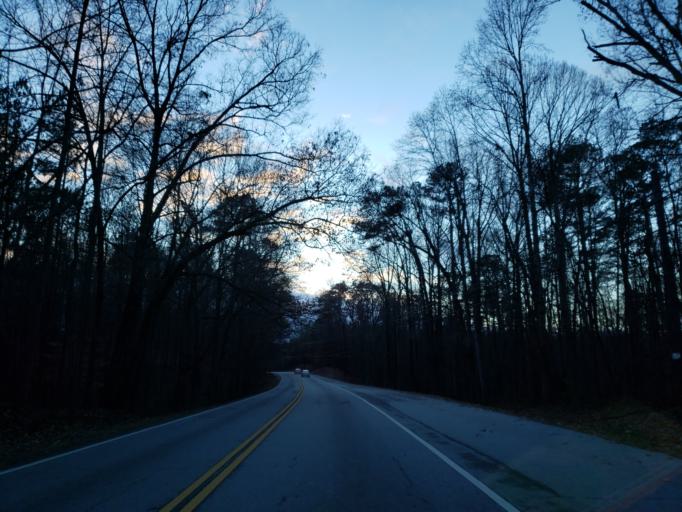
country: US
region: Georgia
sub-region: Fulton County
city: Union City
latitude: 33.6980
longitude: -84.5836
